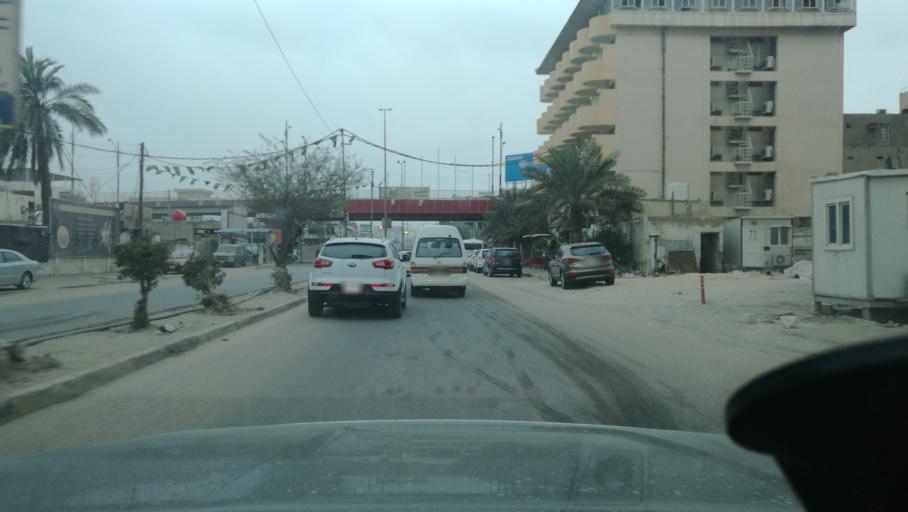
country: IQ
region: Basra Governorate
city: Al Basrah al Qadimah
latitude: 30.5072
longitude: 47.8377
